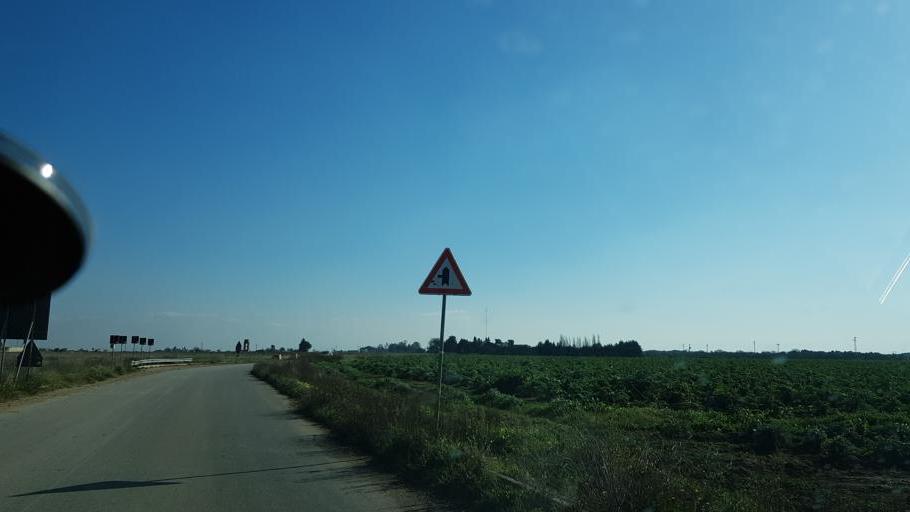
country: IT
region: Apulia
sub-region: Provincia di Brindisi
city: Brindisi
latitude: 40.6476
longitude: 17.8639
